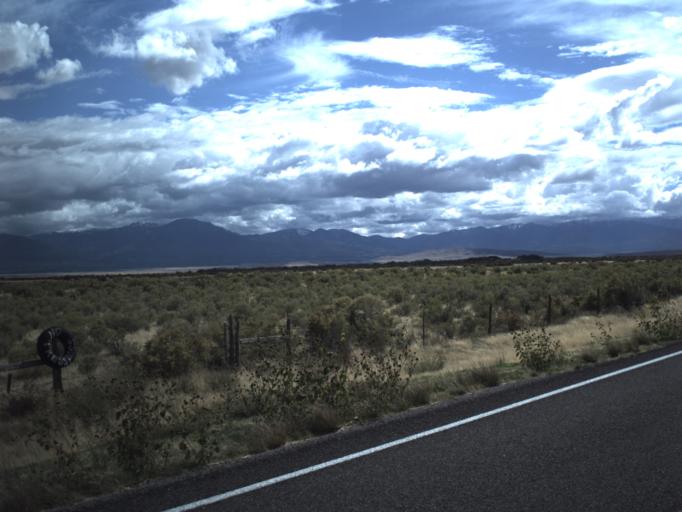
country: US
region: Utah
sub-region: Millard County
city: Fillmore
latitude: 39.1480
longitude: -112.4098
